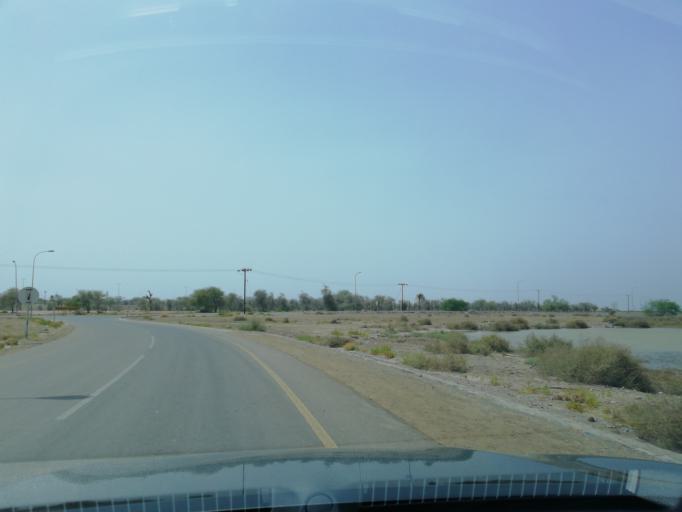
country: OM
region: Al Batinah
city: Shinas
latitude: 24.7535
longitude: 56.4668
